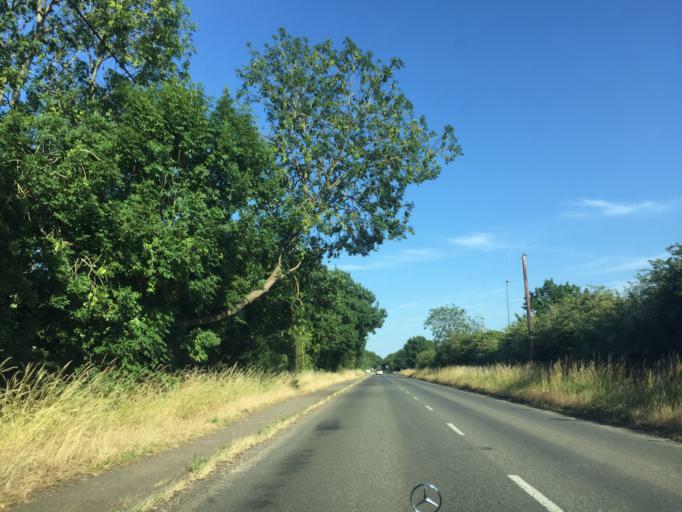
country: GB
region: England
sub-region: Oxfordshire
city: Chalgrove
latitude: 51.7276
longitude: -1.0627
